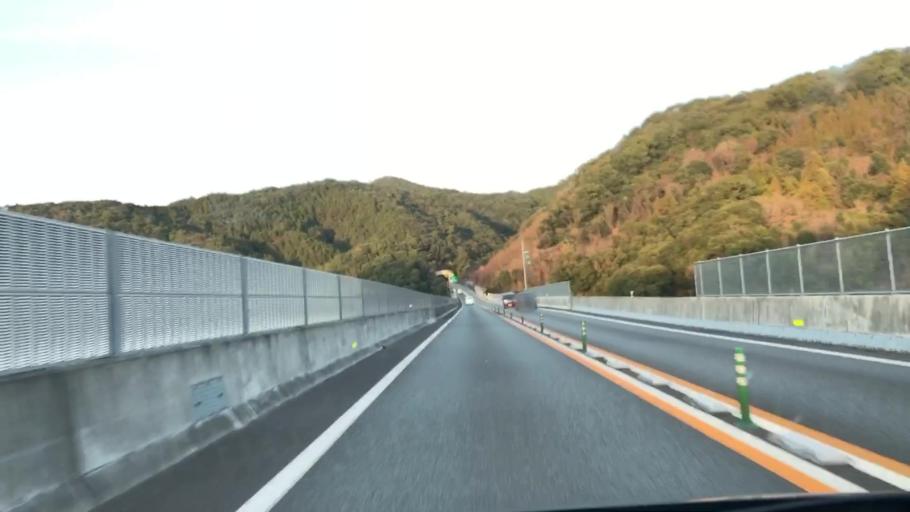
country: JP
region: Kumamoto
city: Minamata
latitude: 32.2787
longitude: 130.4977
